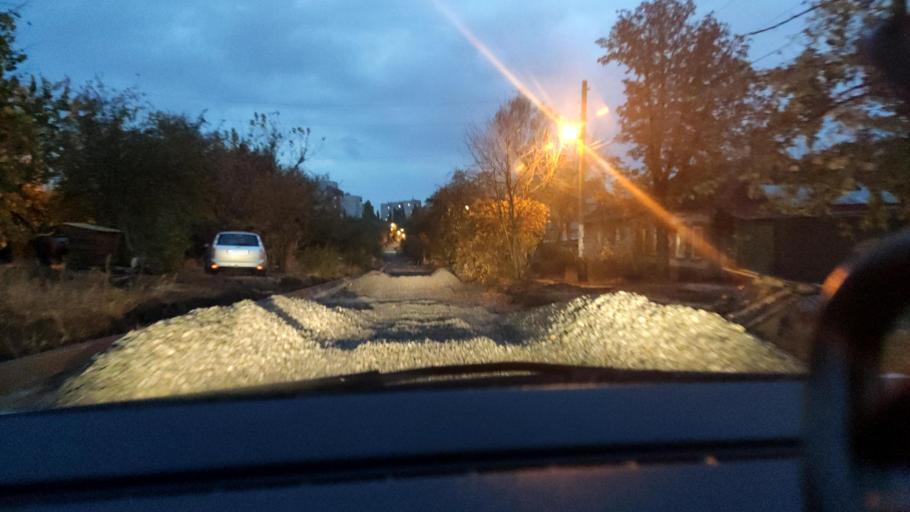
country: RU
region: Voronezj
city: Voronezh
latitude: 51.6929
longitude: 39.1971
